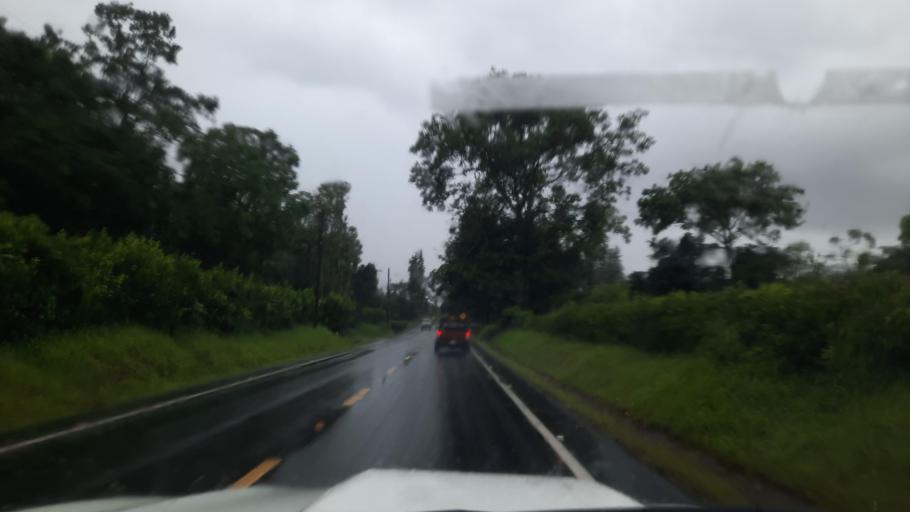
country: PA
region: Chiriqui
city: Sortova
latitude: 8.5644
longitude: -82.6298
